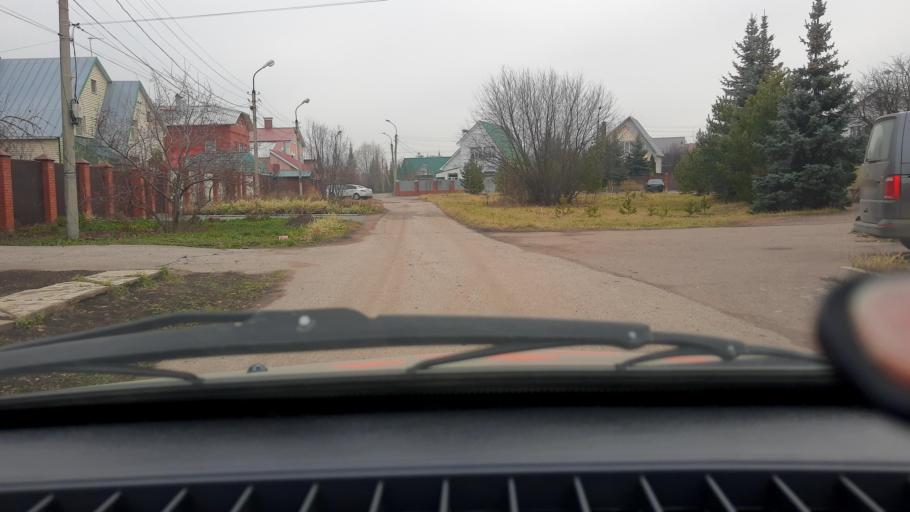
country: RU
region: Bashkortostan
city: Mikhaylovka
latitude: 54.7929
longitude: 55.9420
